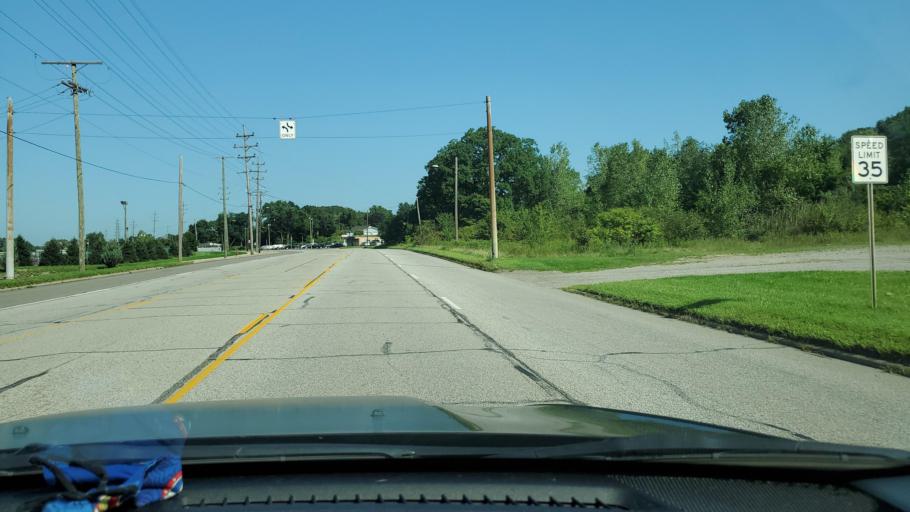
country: US
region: Ohio
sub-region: Trumbull County
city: Girard
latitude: 41.1371
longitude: -80.6878
